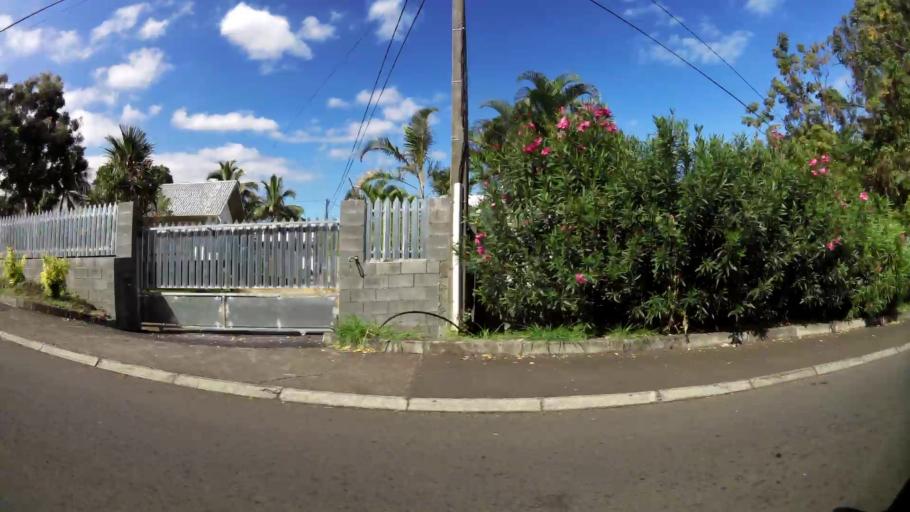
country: RE
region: Reunion
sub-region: Reunion
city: Le Tampon
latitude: -21.2877
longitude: 55.5126
